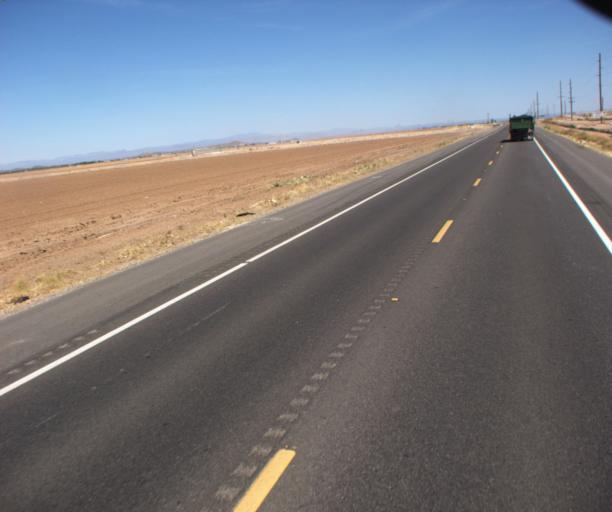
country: US
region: Arizona
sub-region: Pinal County
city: Blackwater
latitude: 33.0025
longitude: -111.5805
